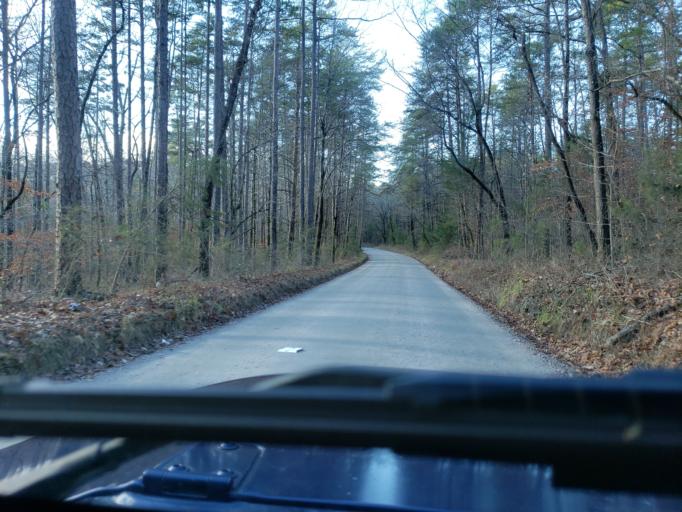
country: US
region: North Carolina
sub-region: Cleveland County
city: Kings Mountain
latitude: 35.1568
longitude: -81.3317
